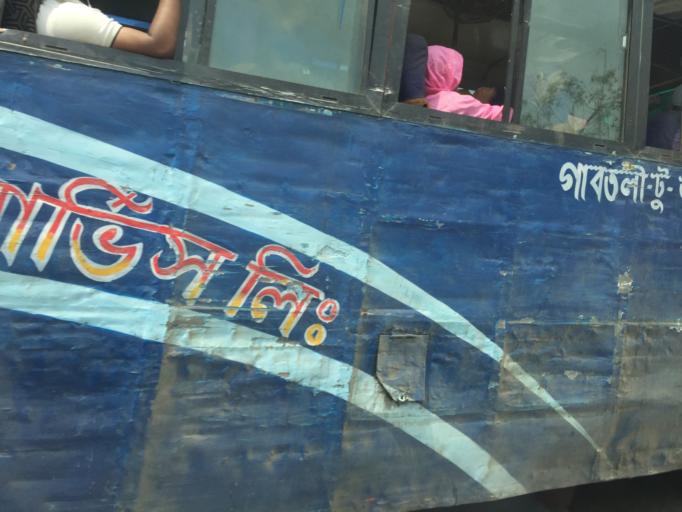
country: BD
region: Dhaka
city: Tungi
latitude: 23.8203
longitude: 90.3954
